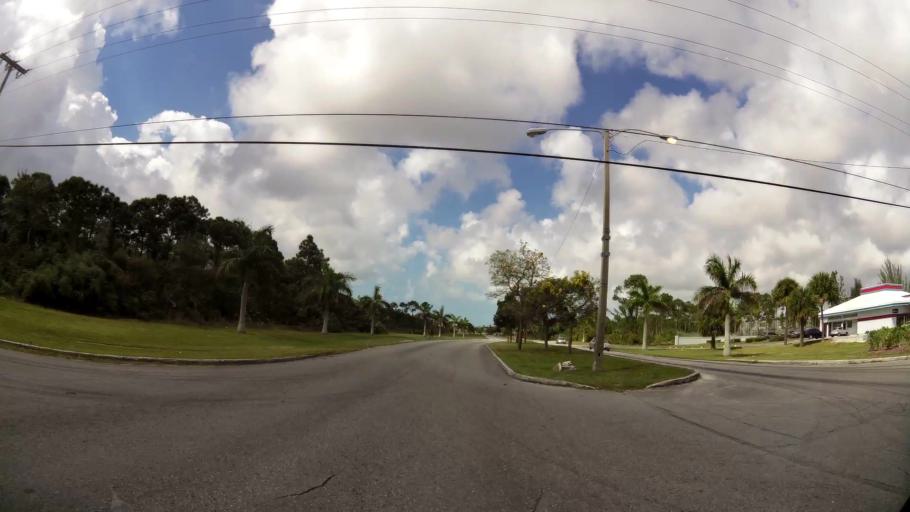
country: BS
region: Freeport
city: Freeport
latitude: 26.5391
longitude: -78.6955
